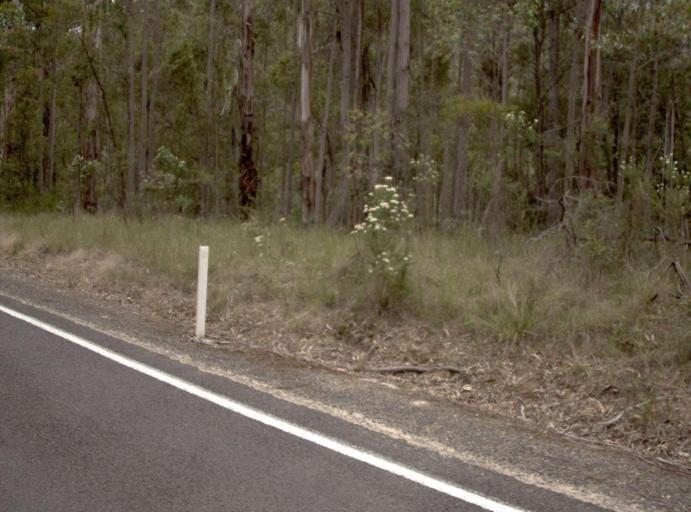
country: AU
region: New South Wales
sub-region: Bombala
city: Bombala
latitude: -37.4206
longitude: 149.2014
